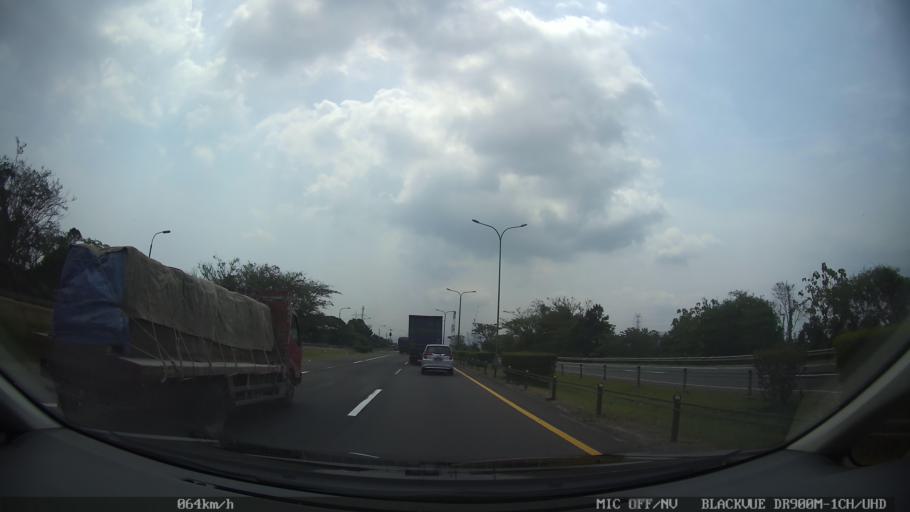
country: ID
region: Banten
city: Bojonegara
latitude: -6.0207
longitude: 106.0912
